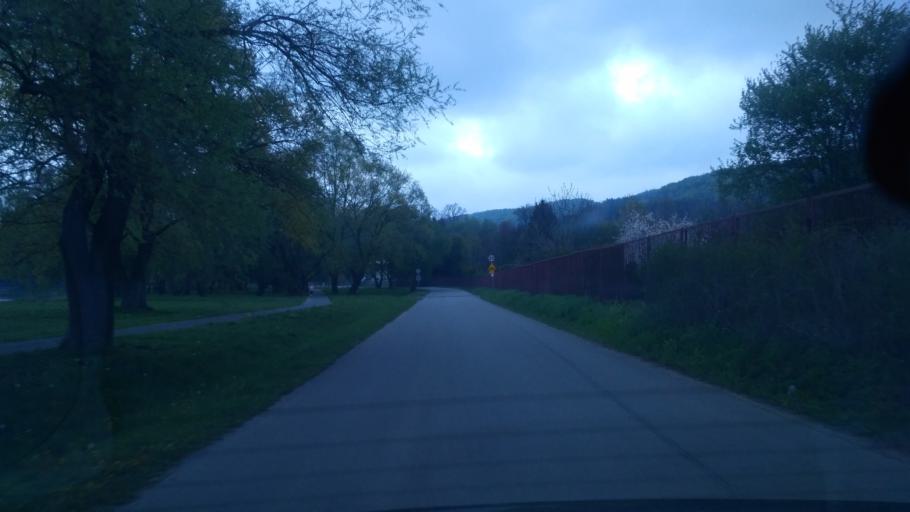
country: PL
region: Subcarpathian Voivodeship
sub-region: Powiat sanocki
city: Sanok
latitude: 49.5710
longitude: 22.2086
